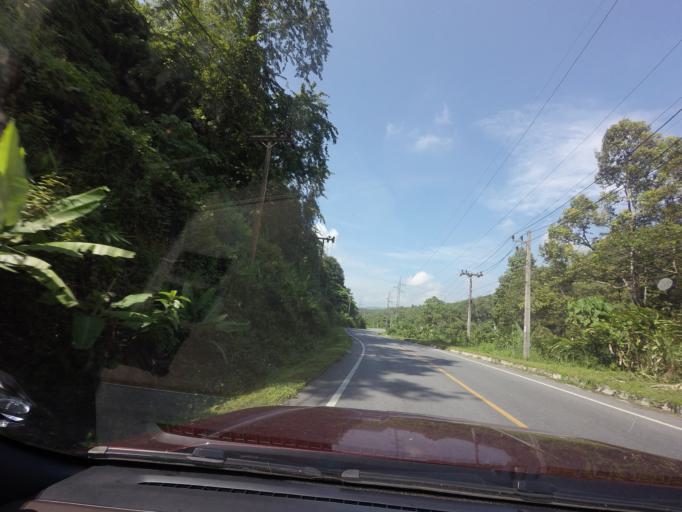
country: TH
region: Yala
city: Betong
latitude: 5.8952
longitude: 101.1460
